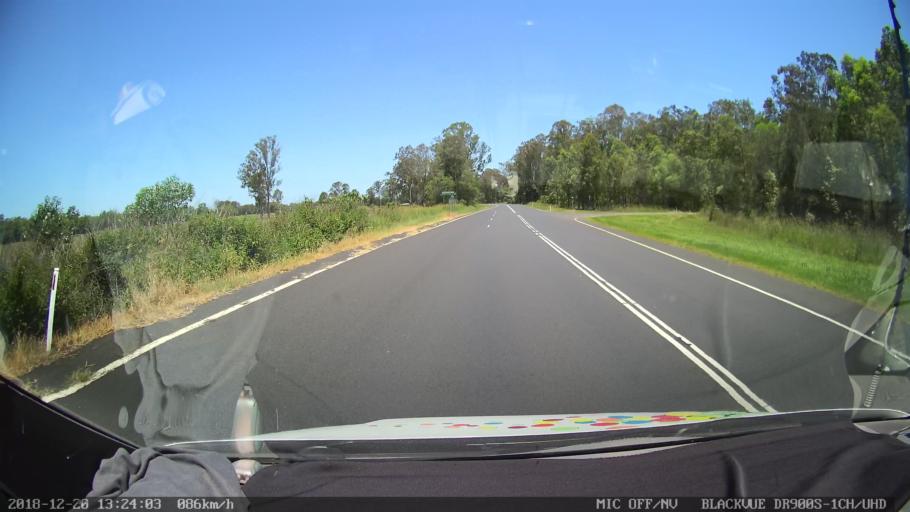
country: AU
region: New South Wales
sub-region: Richmond Valley
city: Casino
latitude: -29.1122
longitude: 153.0006
